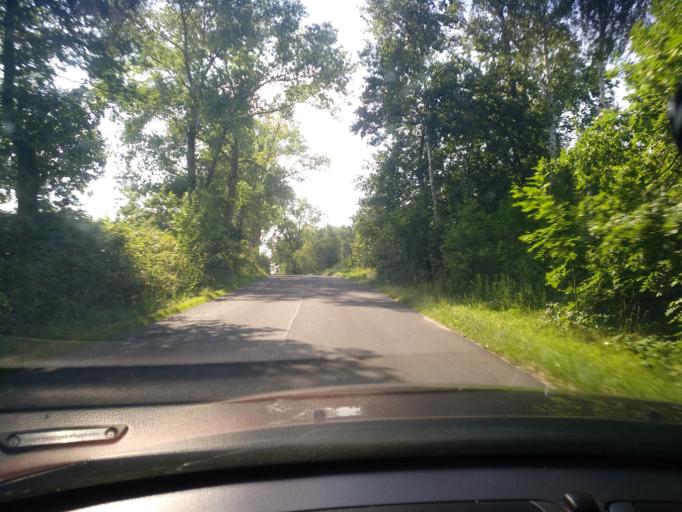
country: PL
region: Lower Silesian Voivodeship
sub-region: Powiat lubanski
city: Lesna
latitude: 51.0263
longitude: 15.2891
